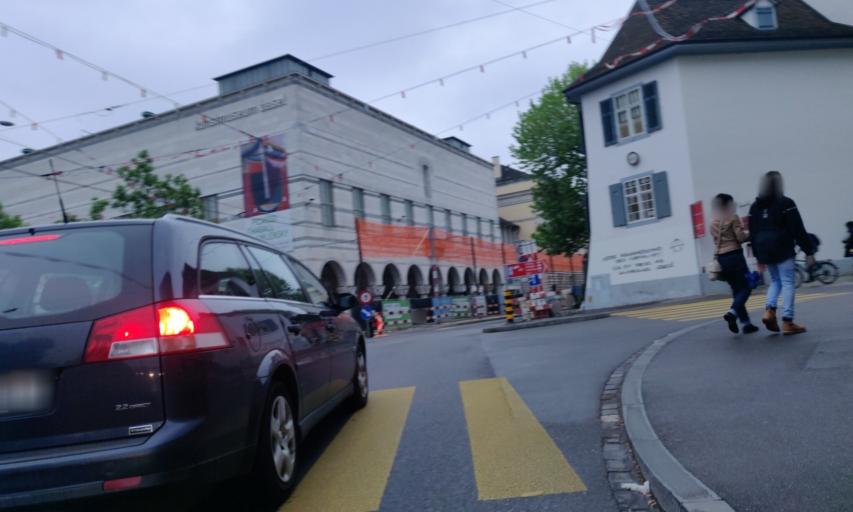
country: CH
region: Basel-City
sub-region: Basel-Stadt
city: Basel
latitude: 47.5549
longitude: 7.5947
